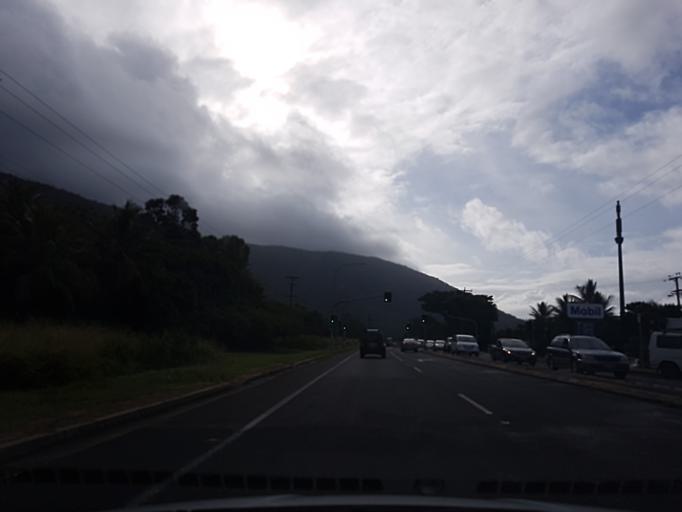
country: AU
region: Queensland
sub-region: Cairns
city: Palm Cove
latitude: -16.7649
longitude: 145.6680
